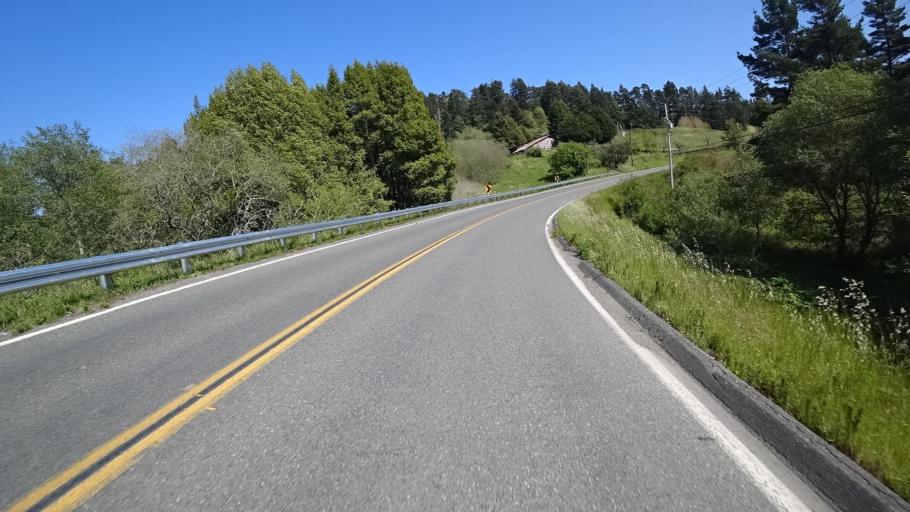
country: US
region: California
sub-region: Humboldt County
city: Hydesville
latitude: 40.5569
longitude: -124.1058
